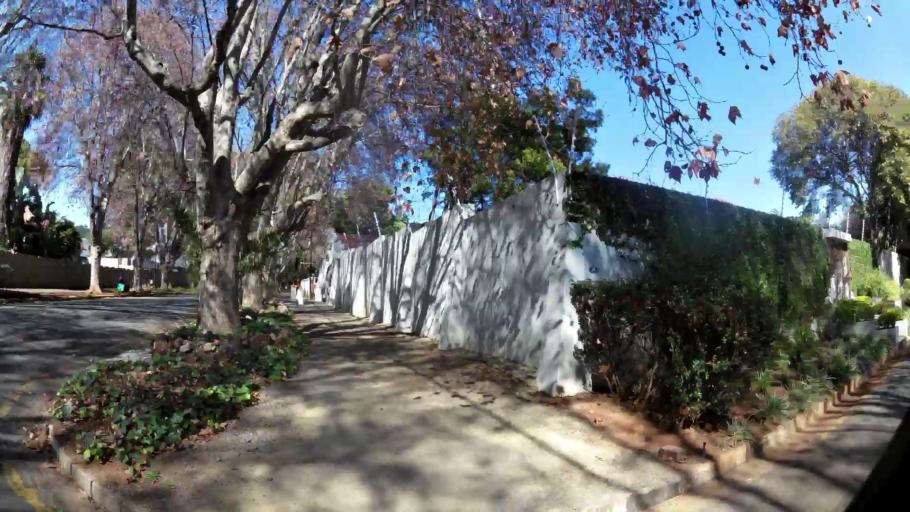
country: ZA
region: Gauteng
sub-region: City of Johannesburg Metropolitan Municipality
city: Johannesburg
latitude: -26.1706
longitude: 28.0376
